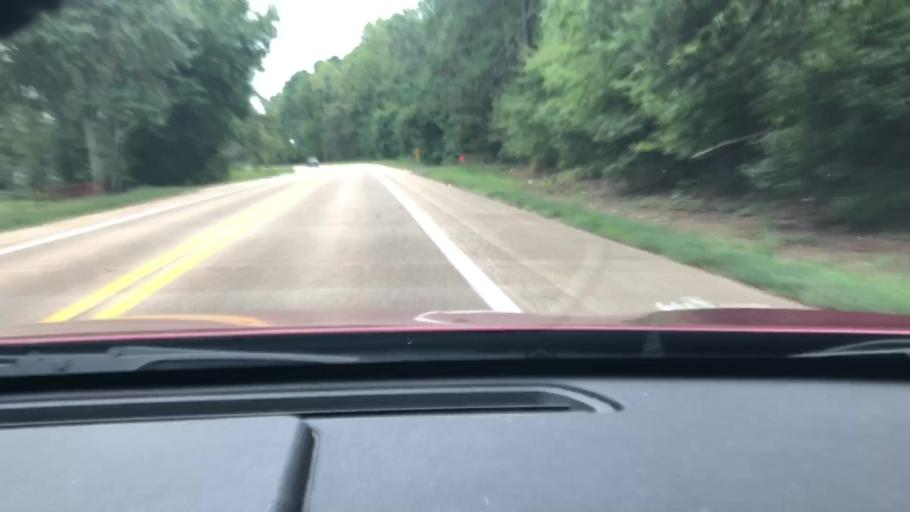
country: US
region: Arkansas
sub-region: Miller County
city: Texarkana
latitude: 33.4196
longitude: -93.8244
